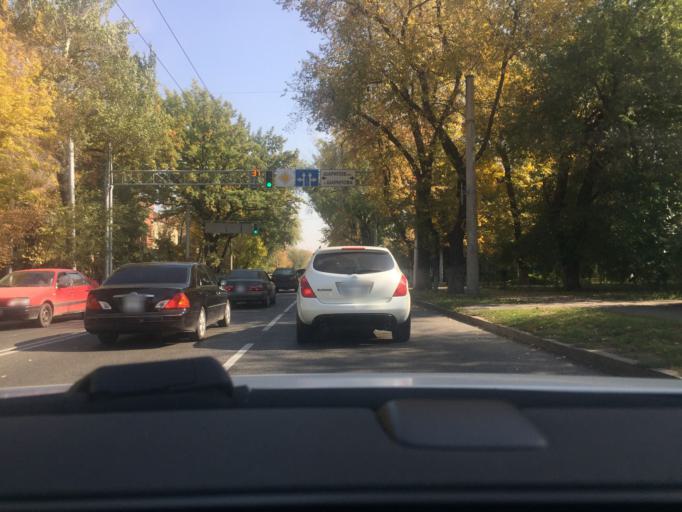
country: KZ
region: Almaty Qalasy
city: Almaty
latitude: 43.2583
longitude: 76.9208
